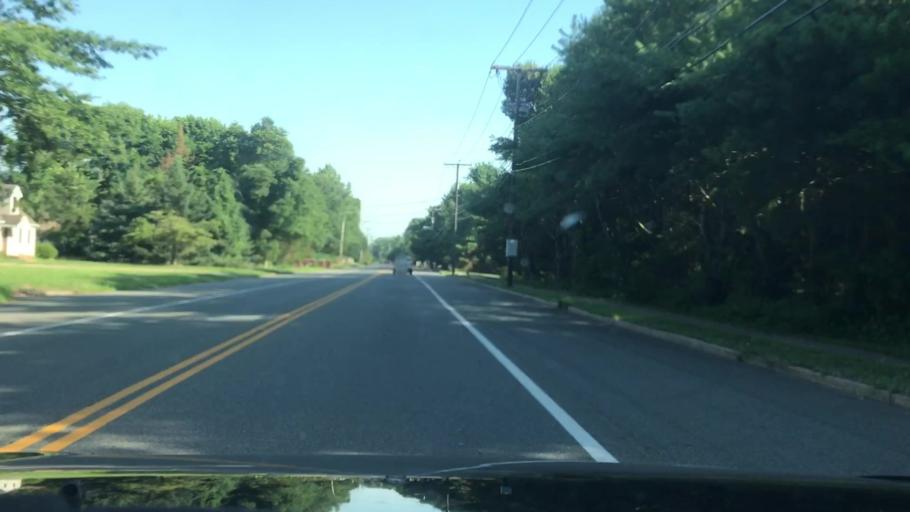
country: US
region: New Jersey
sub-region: Ocean County
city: Leisure Village
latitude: 40.0252
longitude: -74.2007
